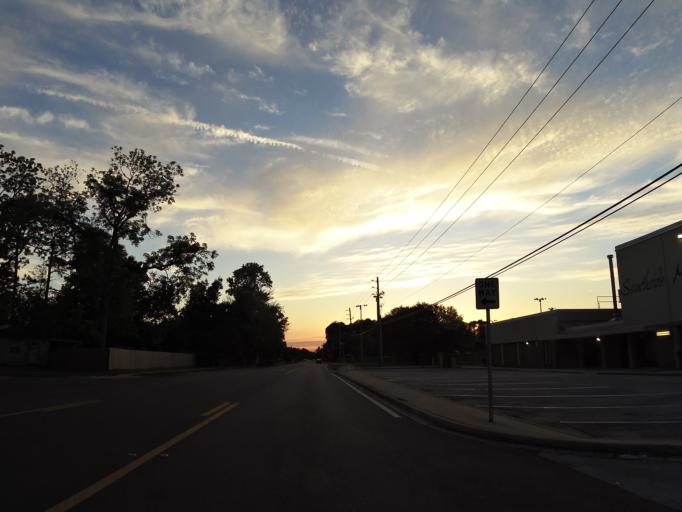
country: US
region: Florida
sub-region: Duval County
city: Jacksonville
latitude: 30.2701
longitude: -81.5960
